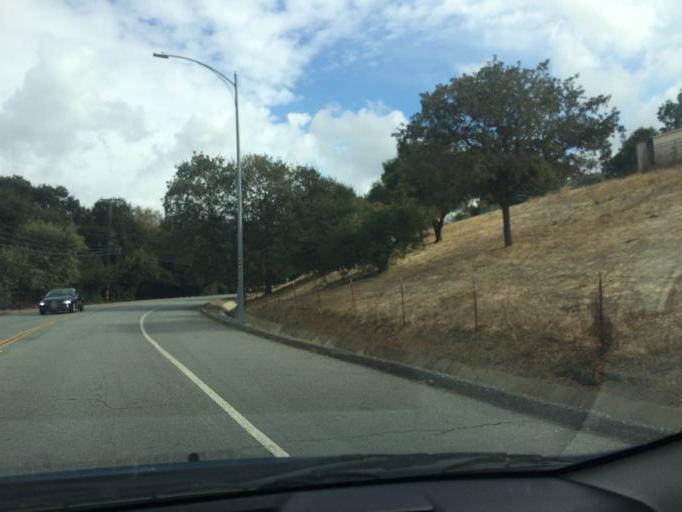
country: US
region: California
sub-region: Santa Clara County
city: Seven Trees
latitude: 37.2796
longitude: -121.7558
